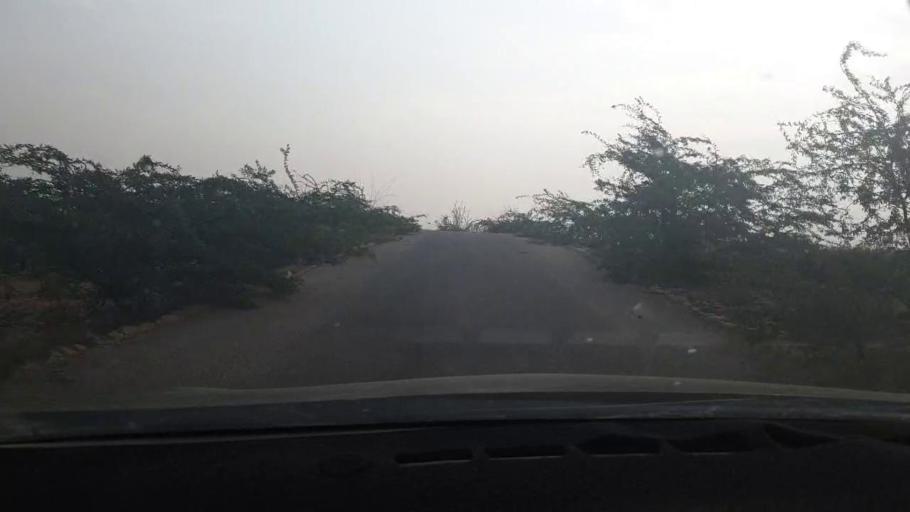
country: PK
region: Sindh
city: Malir Cantonment
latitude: 24.9517
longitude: 67.4330
